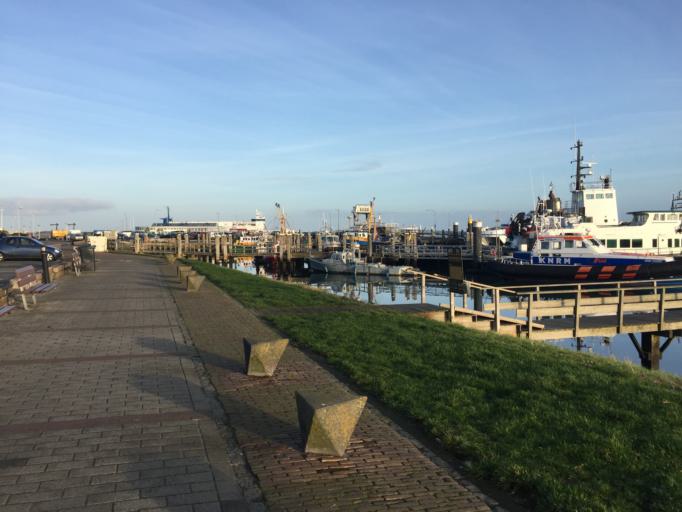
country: NL
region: Friesland
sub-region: Gemeente Terschelling
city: West-Terschelling
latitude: 53.3564
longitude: 5.2135
